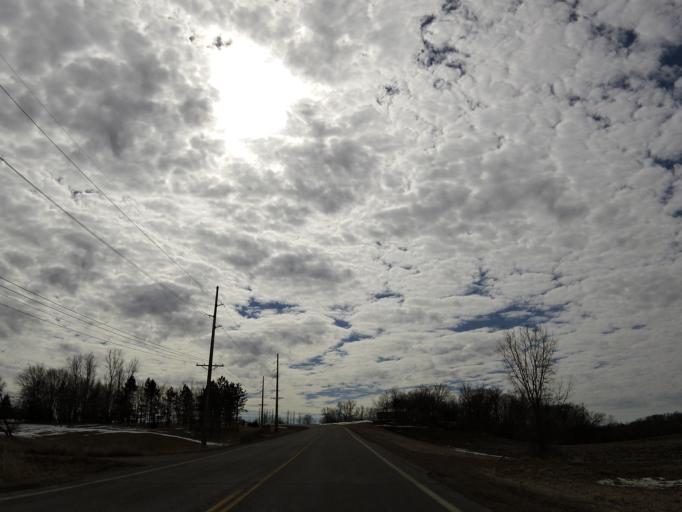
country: US
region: Minnesota
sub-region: Scott County
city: Jordan
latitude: 44.6253
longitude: -93.5626
